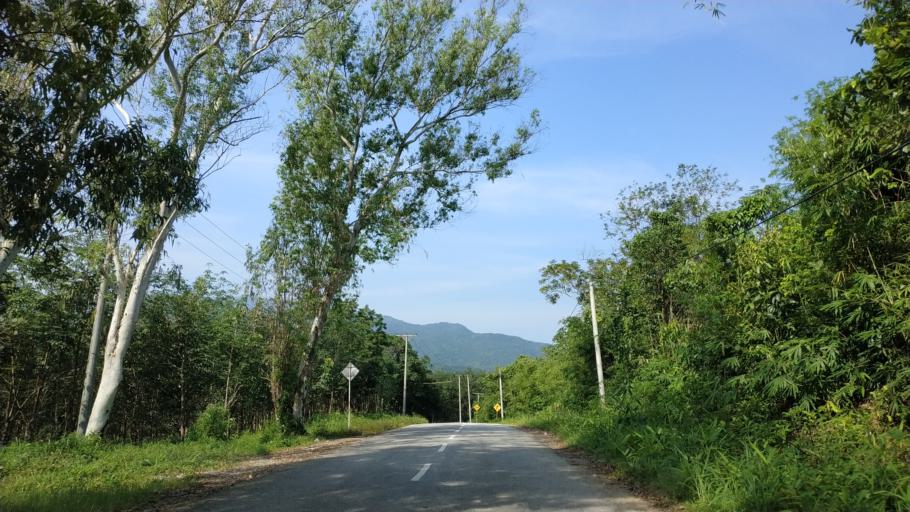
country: MM
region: Tanintharyi
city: Dawei
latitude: 14.5984
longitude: 98.0851
